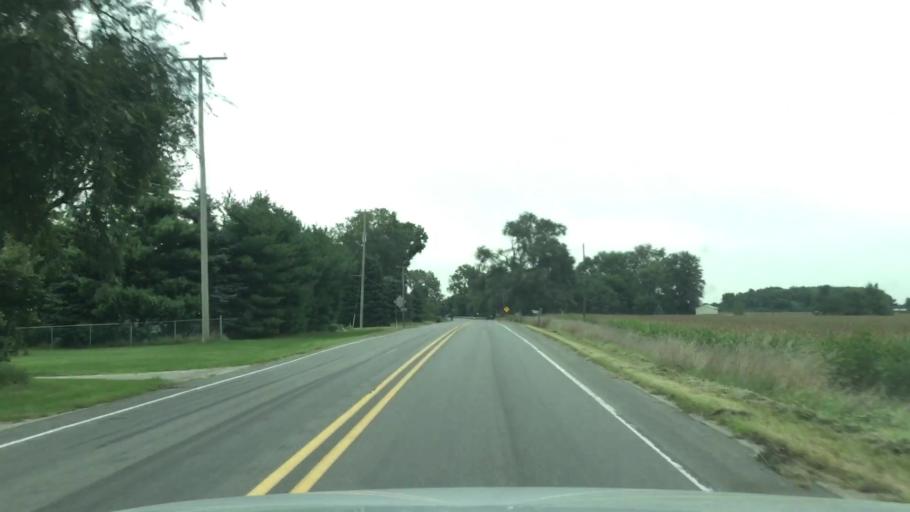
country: US
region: Michigan
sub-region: Washtenaw County
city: Milan
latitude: 42.1248
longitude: -83.6952
